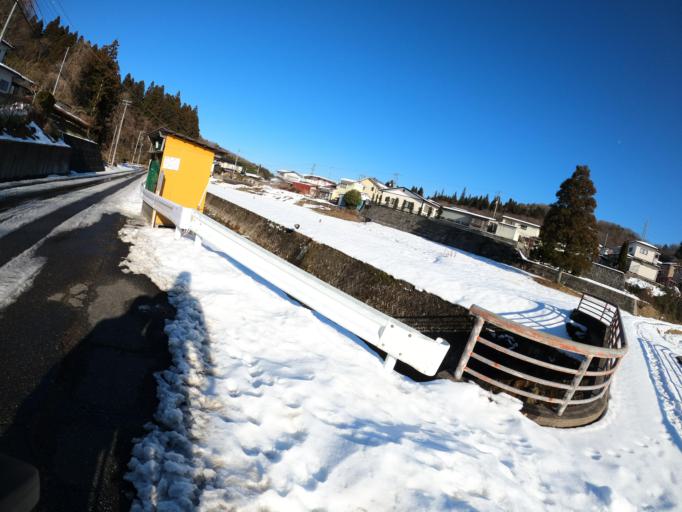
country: JP
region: Iwate
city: Ichinoseki
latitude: 38.9097
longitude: 141.1211
